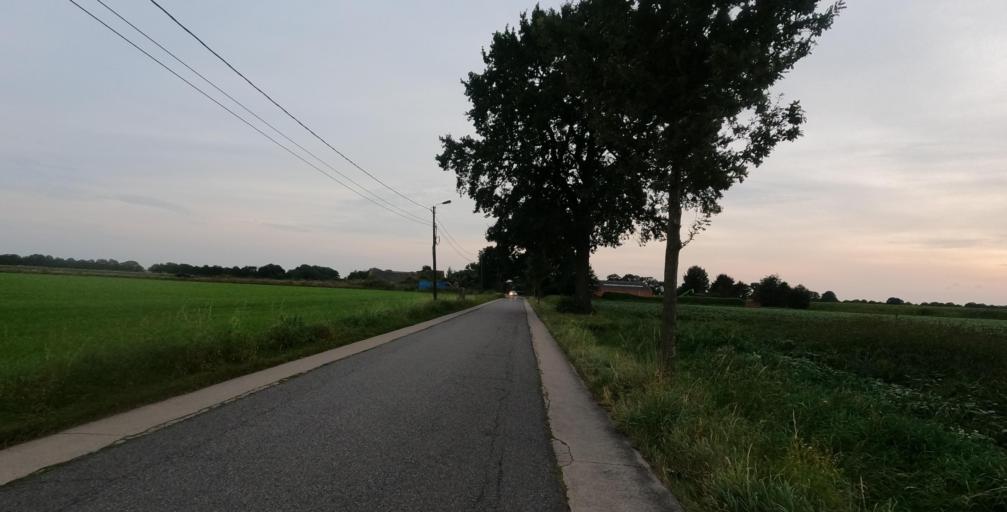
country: BE
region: Flanders
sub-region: Provincie Antwerpen
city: Essen
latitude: 51.4426
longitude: 4.4925
